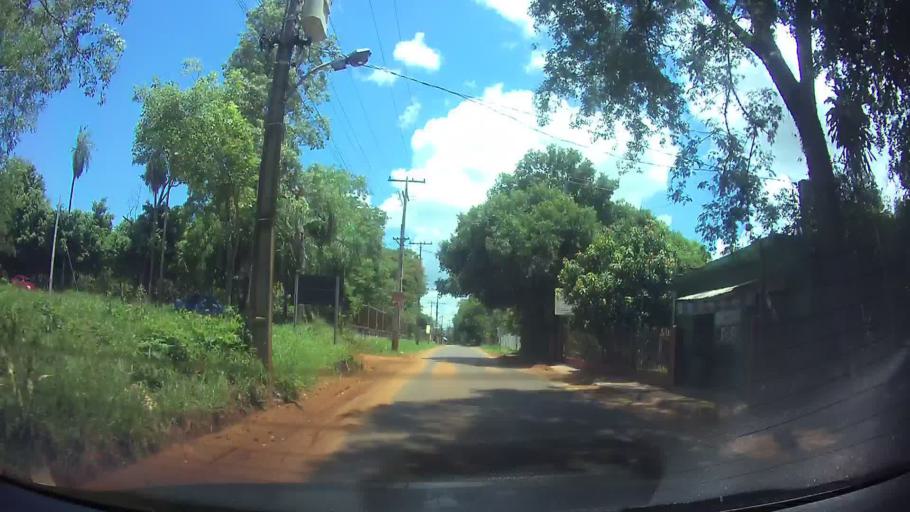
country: PY
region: Central
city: Itaugua
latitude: -25.3759
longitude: -57.3662
